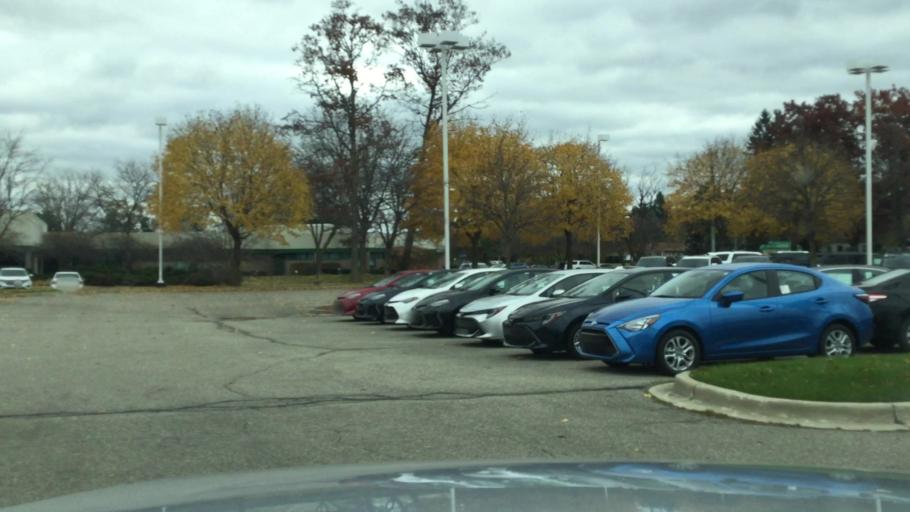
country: US
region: Michigan
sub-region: Oakland County
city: Keego Harbor
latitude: 42.6512
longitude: -83.3675
